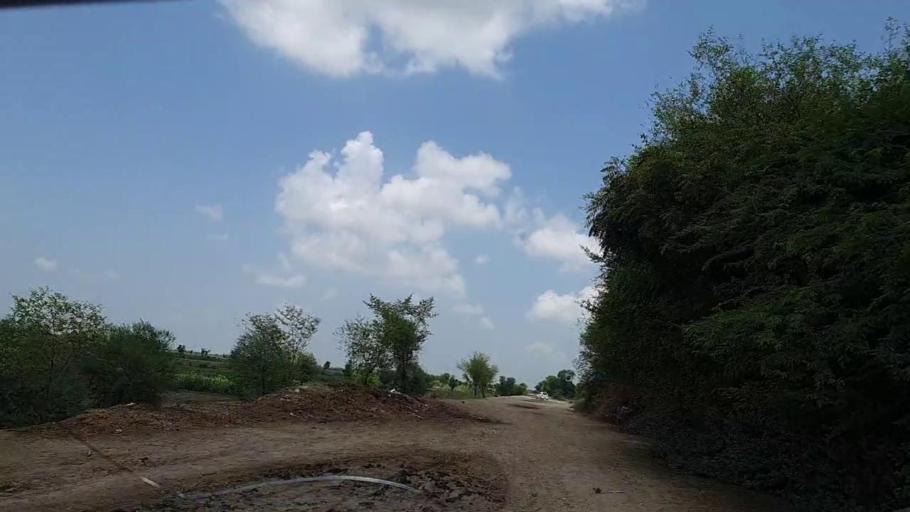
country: PK
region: Sindh
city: Tharu Shah
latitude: 26.9601
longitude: 68.0284
